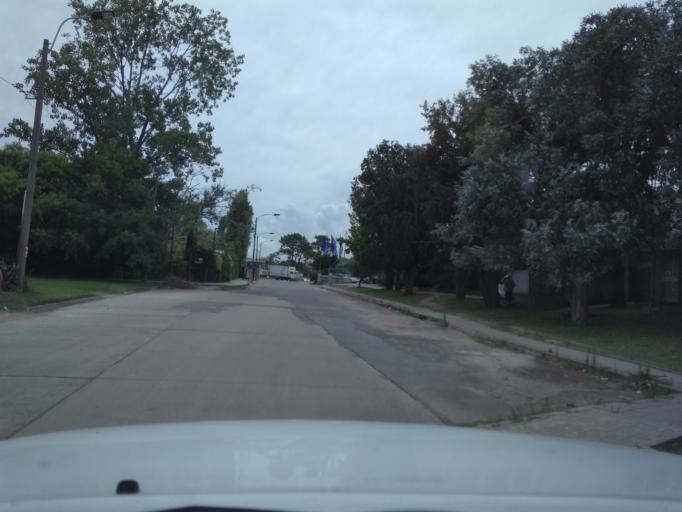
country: UY
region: Canelones
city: Paso de Carrasco
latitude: -34.8785
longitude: -56.0574
